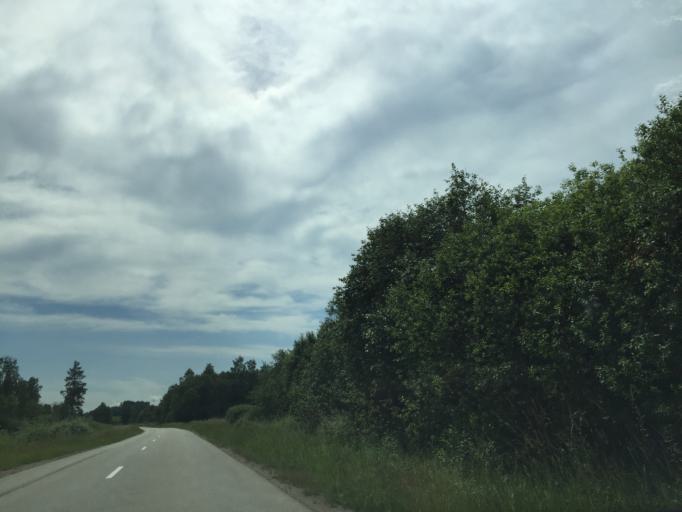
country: LV
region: Engure
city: Smarde
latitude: 57.0415
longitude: 23.2577
